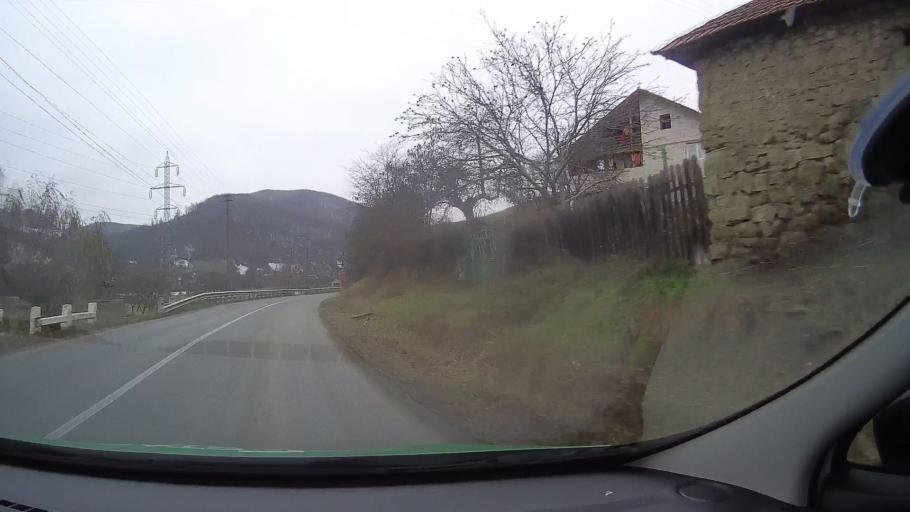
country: RO
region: Alba
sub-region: Comuna Metes
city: Metes
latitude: 46.0991
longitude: 23.4571
